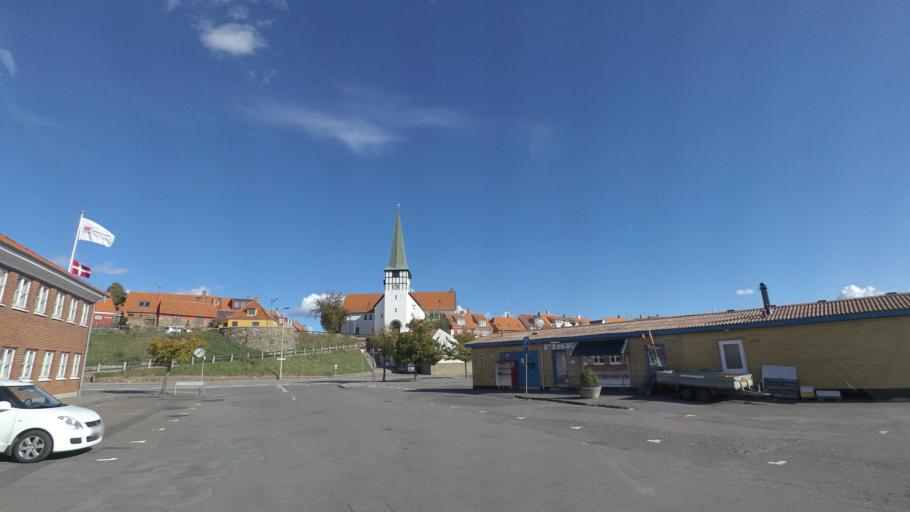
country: DK
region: Capital Region
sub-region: Bornholm Kommune
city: Ronne
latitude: 55.0989
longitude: 14.6955
